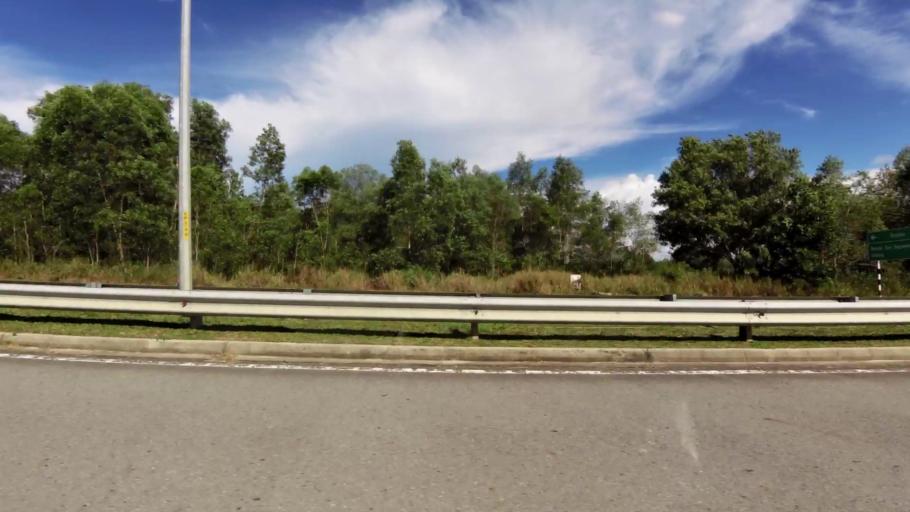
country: BN
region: Brunei and Muara
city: Bandar Seri Begawan
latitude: 4.9753
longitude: 114.9312
